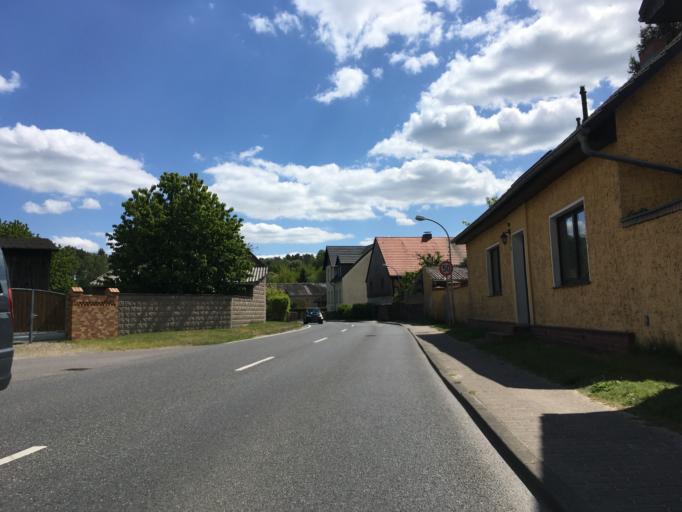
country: DE
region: Brandenburg
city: Marienwerder
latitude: 52.7902
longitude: 13.5521
